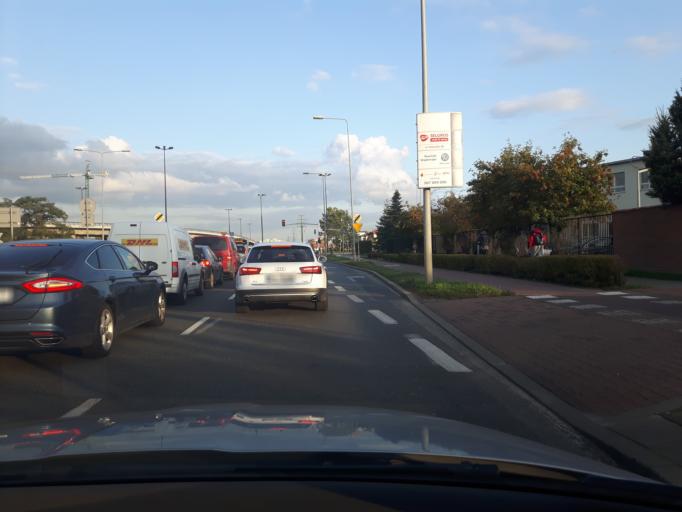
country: PL
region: Masovian Voivodeship
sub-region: Warszawa
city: Ursynow
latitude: 52.1531
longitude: 21.0157
